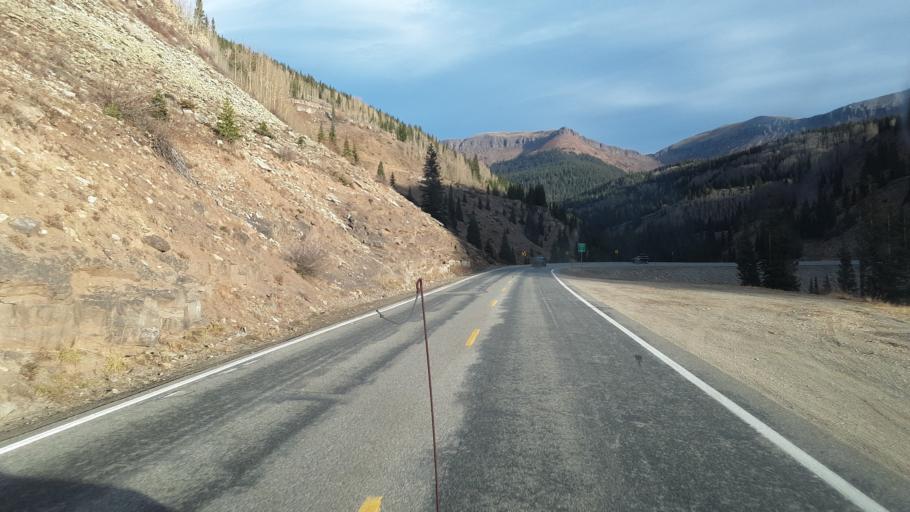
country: US
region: Colorado
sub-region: San Juan County
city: Silverton
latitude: 37.7299
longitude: -107.7511
